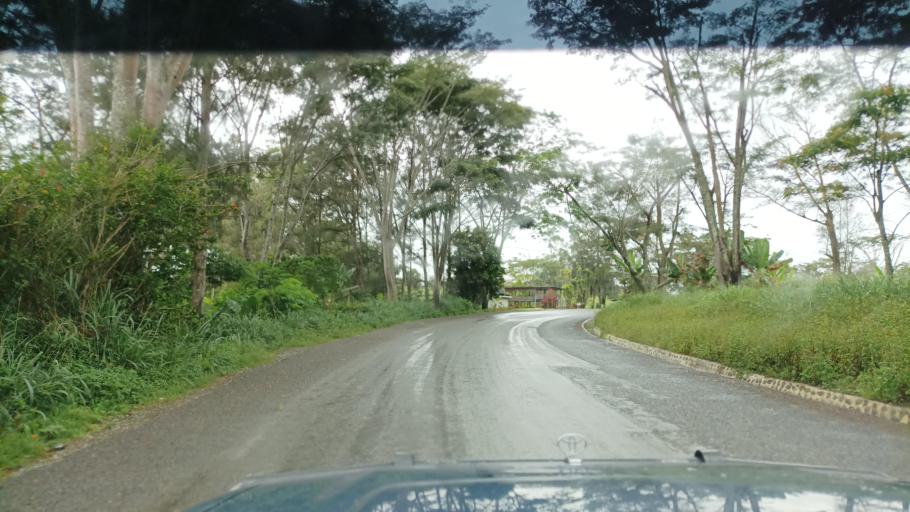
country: PG
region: Jiwaka
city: Minj
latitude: -5.8414
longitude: 144.6202
